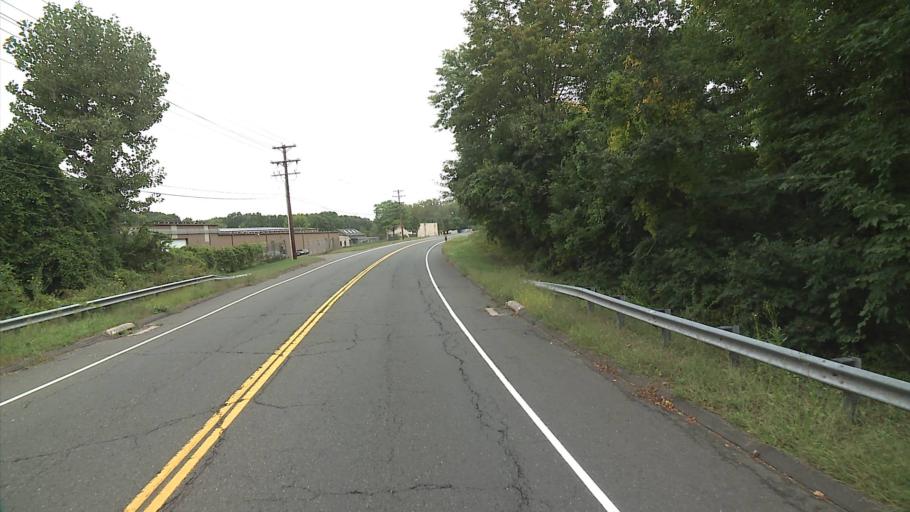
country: US
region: Connecticut
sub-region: Hartford County
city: Windsor Locks
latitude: 41.9420
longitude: -72.6106
